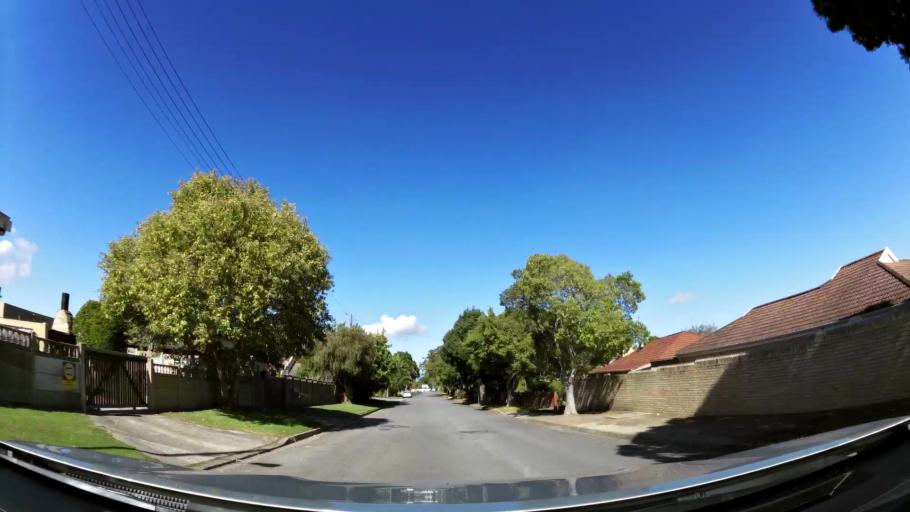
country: ZA
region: Western Cape
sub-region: Eden District Municipality
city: George
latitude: -33.9417
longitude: 22.4719
